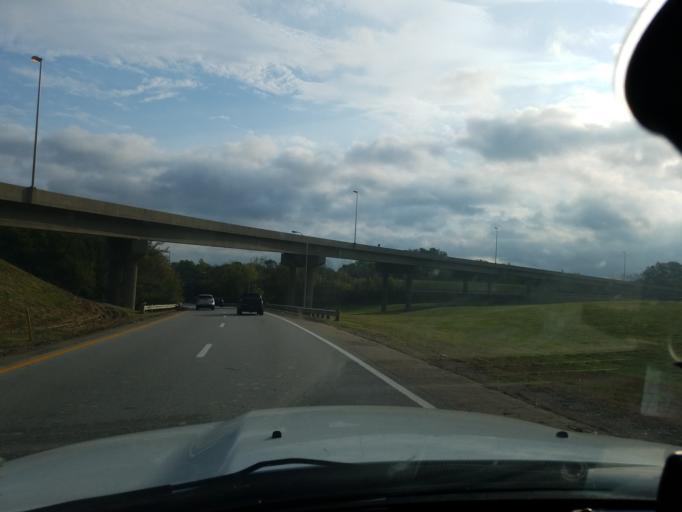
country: US
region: Indiana
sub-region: Floyd County
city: New Albany
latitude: 38.2753
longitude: -85.8111
